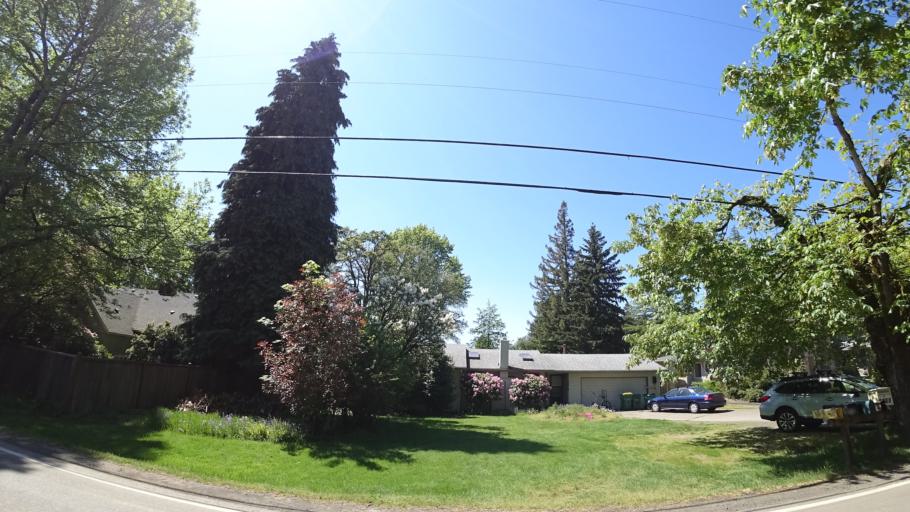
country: US
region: Oregon
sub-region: Washington County
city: Raleigh Hills
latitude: 45.4819
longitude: -122.7609
